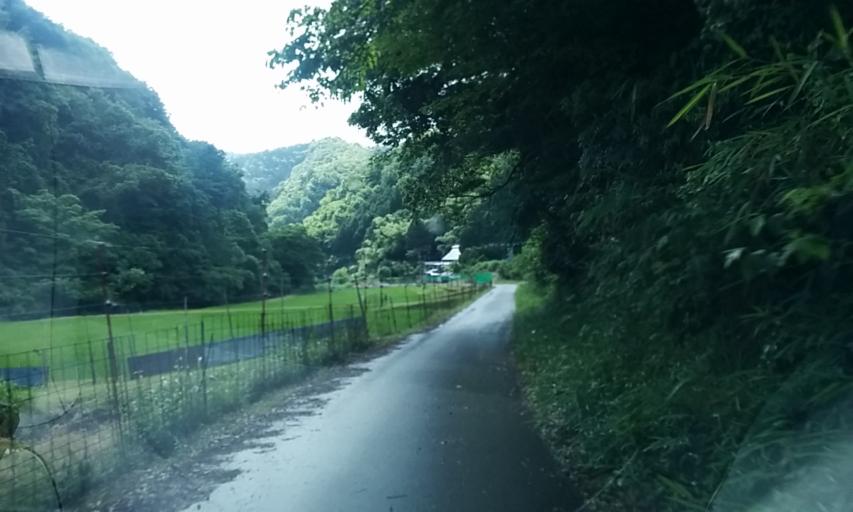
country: JP
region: Kyoto
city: Maizuru
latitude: 35.3931
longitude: 135.2670
